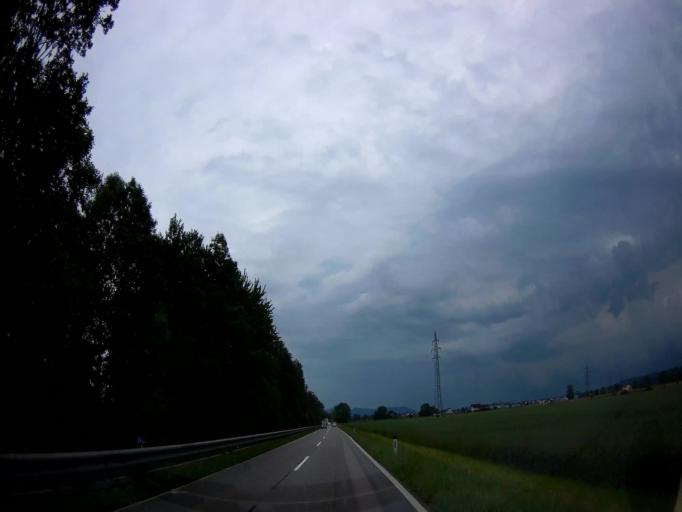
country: AT
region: Upper Austria
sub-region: Politischer Bezirk Braunau am Inn
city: Altheim
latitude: 48.1374
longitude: 13.1386
